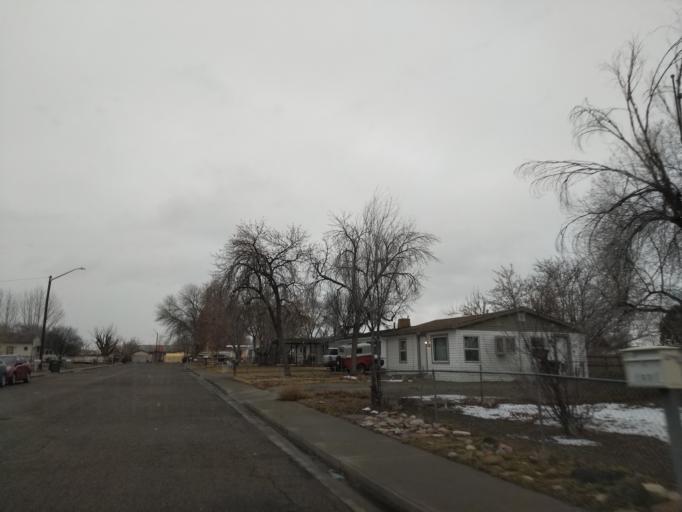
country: US
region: Colorado
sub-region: Mesa County
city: Fruitvale
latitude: 39.0754
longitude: -108.5233
